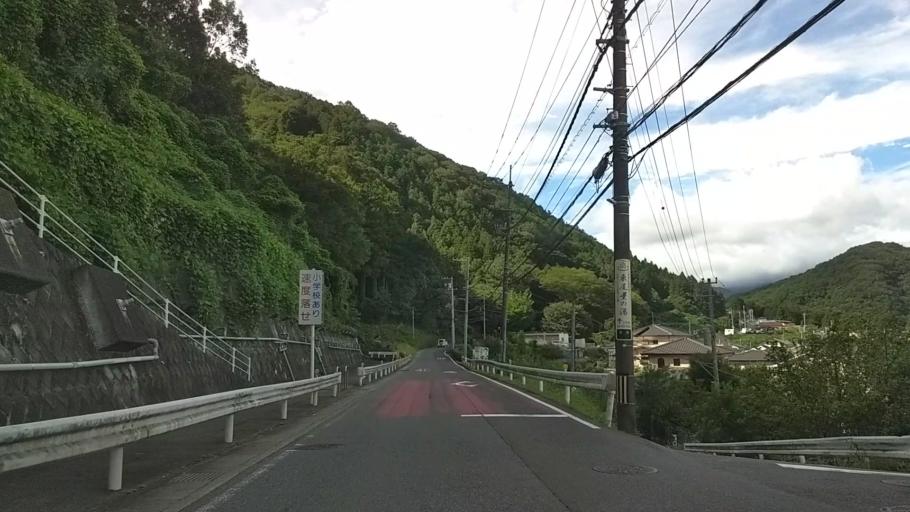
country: JP
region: Yamanashi
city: Uenohara
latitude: 35.6069
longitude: 139.1560
